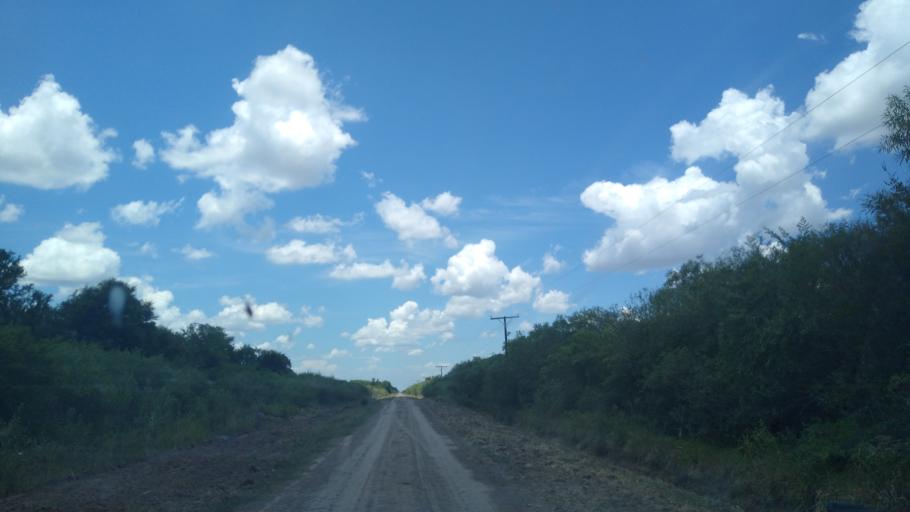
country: AR
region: Chaco
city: Presidencia Roque Saenz Pena
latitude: -26.7405
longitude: -60.3332
